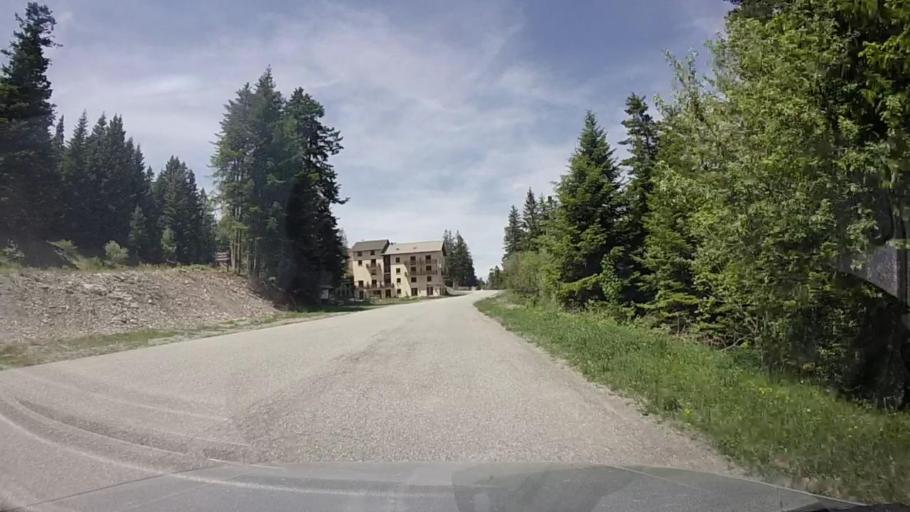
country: FR
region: Provence-Alpes-Cote d'Azur
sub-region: Departement des Alpes-de-Haute-Provence
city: Seyne-les-Alpes
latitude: 44.3468
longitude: 6.2976
